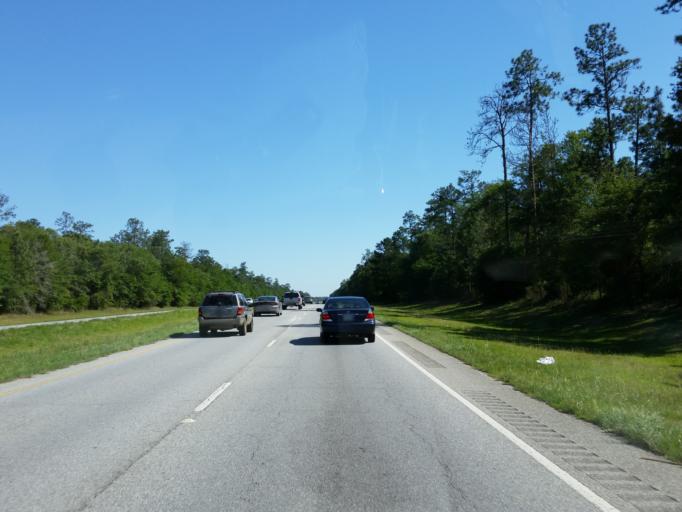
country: US
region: Georgia
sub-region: Lowndes County
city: Valdosta
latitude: 30.8690
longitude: -83.2325
